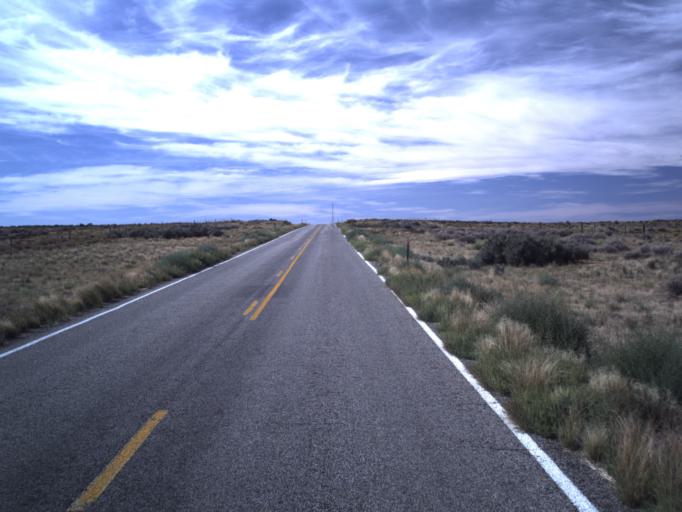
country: US
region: Utah
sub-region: San Juan County
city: Blanding
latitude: 37.3436
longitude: -109.3487
